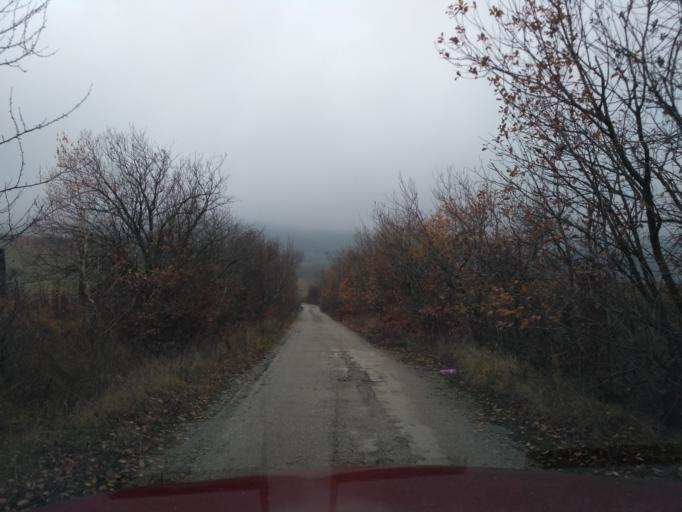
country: SK
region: Kosicky
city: Kosice
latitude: 48.7810
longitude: 21.2144
